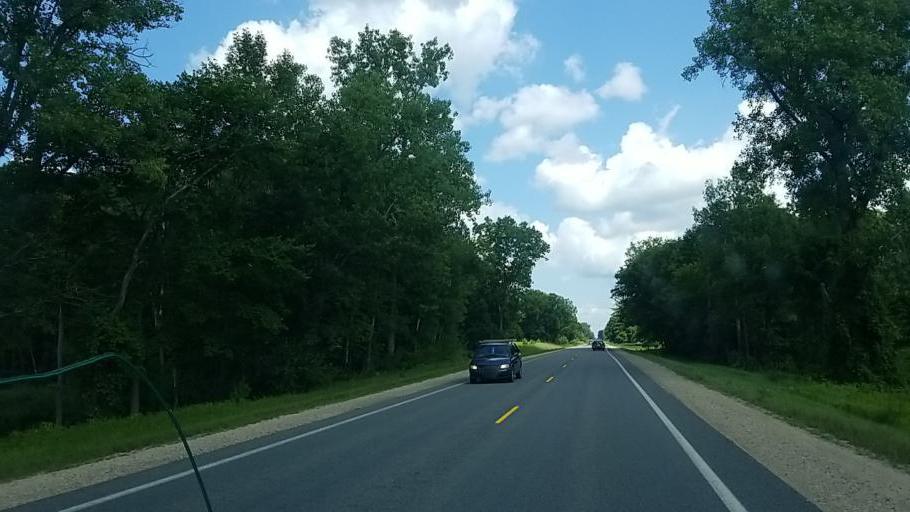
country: US
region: Michigan
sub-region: Newaygo County
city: Newaygo
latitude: 43.3957
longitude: -85.6357
